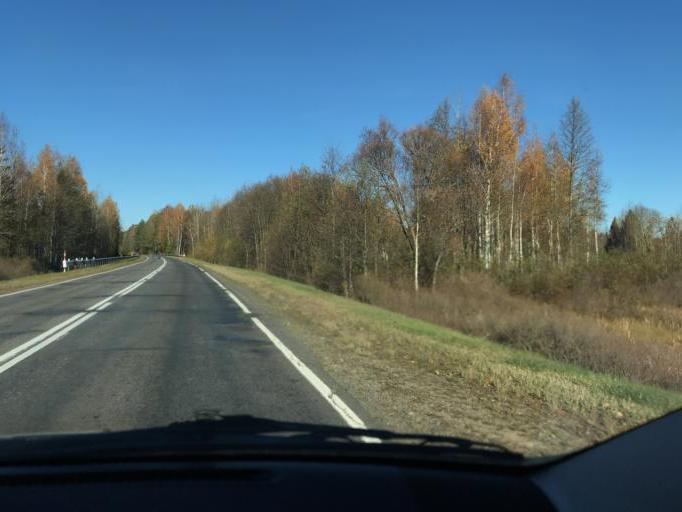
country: BY
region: Vitebsk
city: Polatsk
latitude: 55.4015
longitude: 28.8079
